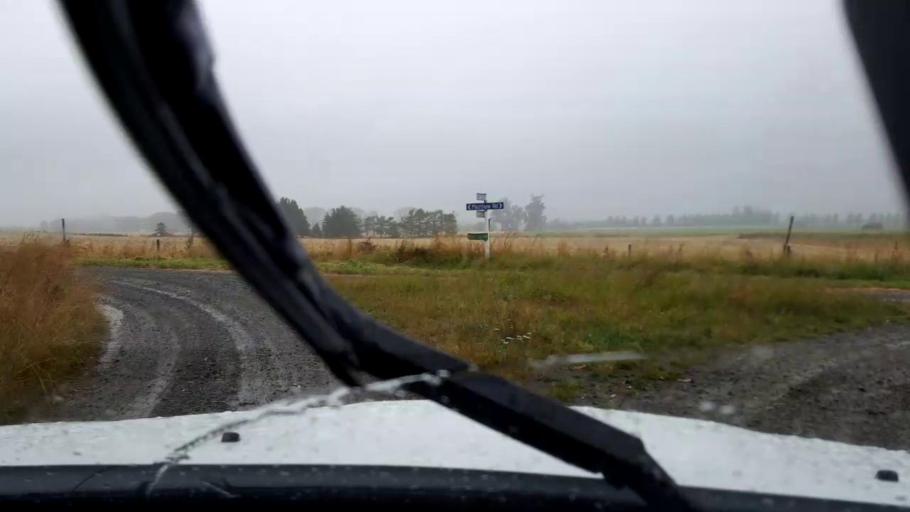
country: NZ
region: Canterbury
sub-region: Timaru District
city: Pleasant Point
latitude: -44.1960
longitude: 171.1045
